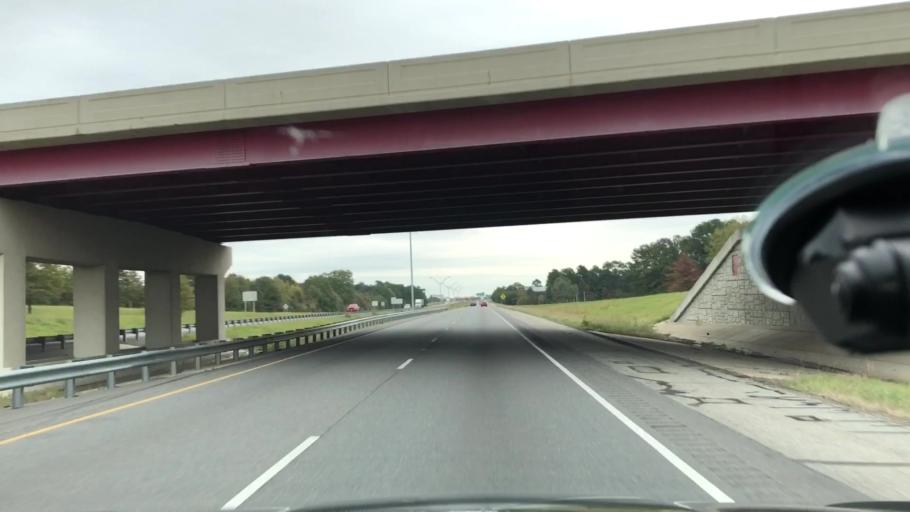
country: US
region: Arkansas
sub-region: Miller County
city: Texarkana
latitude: 33.4757
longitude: -94.0074
